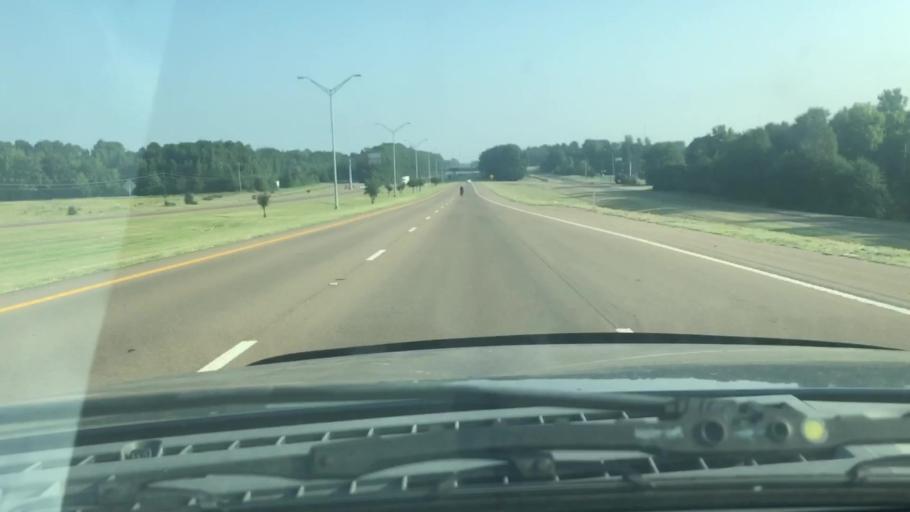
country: US
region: Texas
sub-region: Bowie County
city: Wake Village
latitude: 33.4044
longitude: -94.0975
